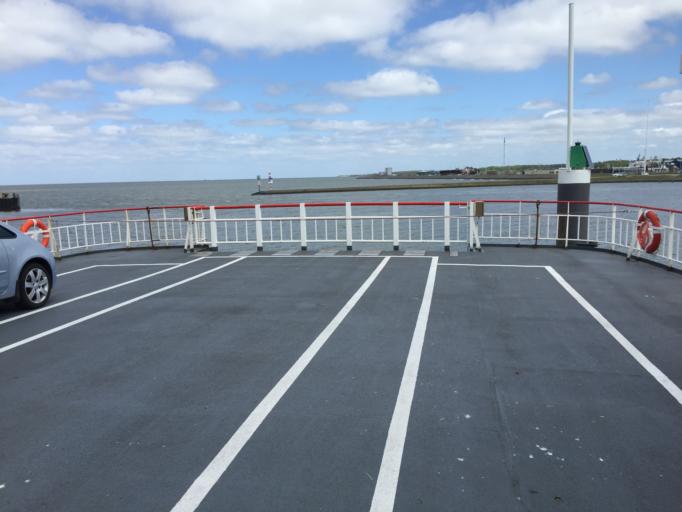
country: NL
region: Friesland
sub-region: Gemeente Dongeradeel
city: Anjum
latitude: 53.4106
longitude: 6.1983
